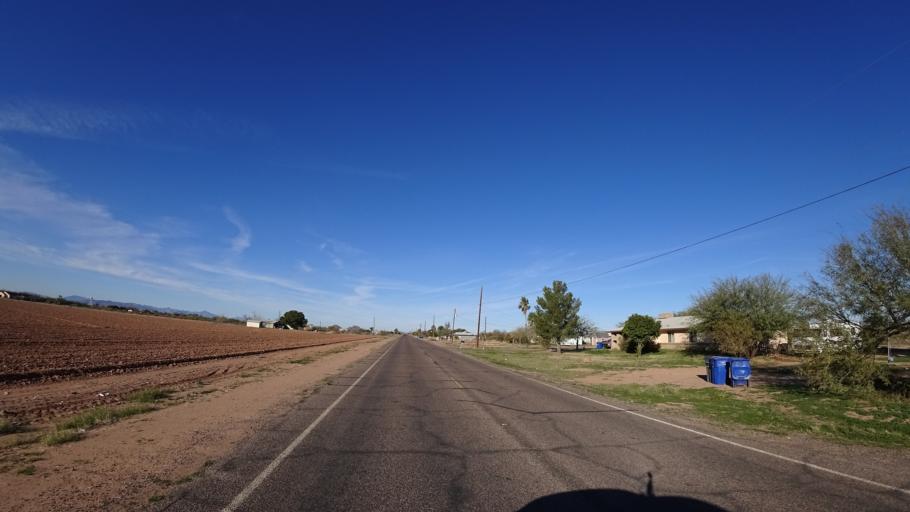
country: US
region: Arizona
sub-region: Maricopa County
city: Scottsdale
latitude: 33.4805
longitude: -111.8511
